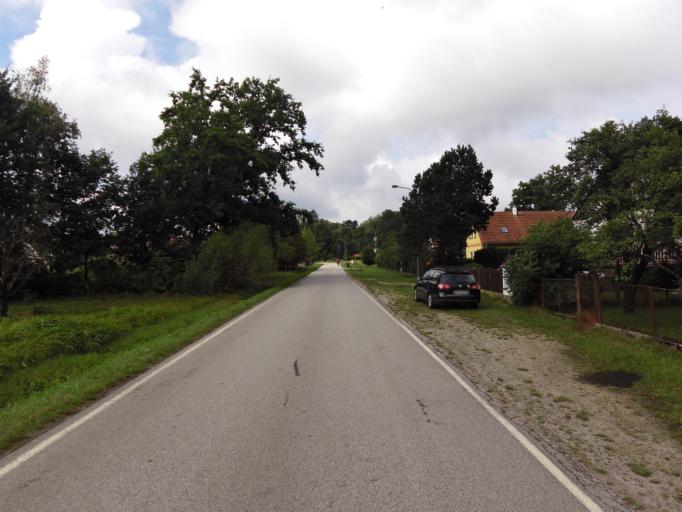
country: CZ
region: Jihocesky
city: Suchdol nad Luznici
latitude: 48.8689
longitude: 14.8760
